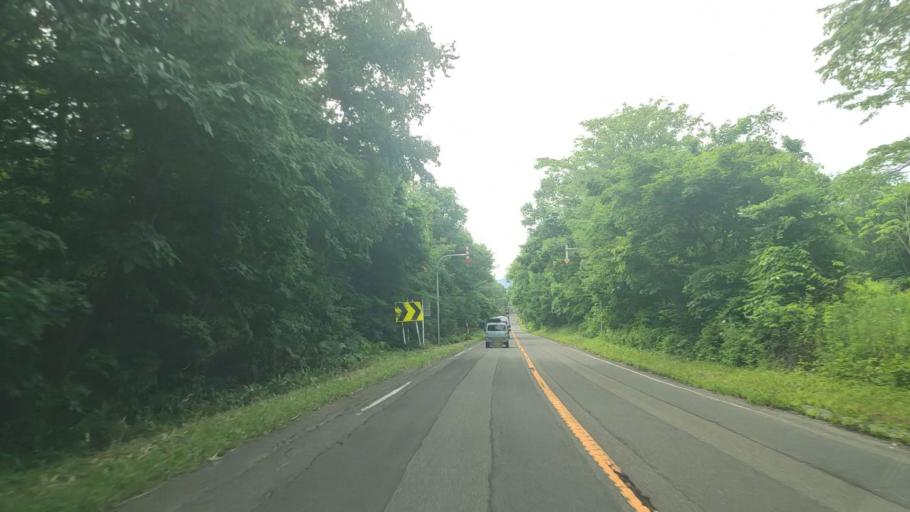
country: JP
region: Hokkaido
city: Chitose
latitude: 42.7914
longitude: 141.5261
